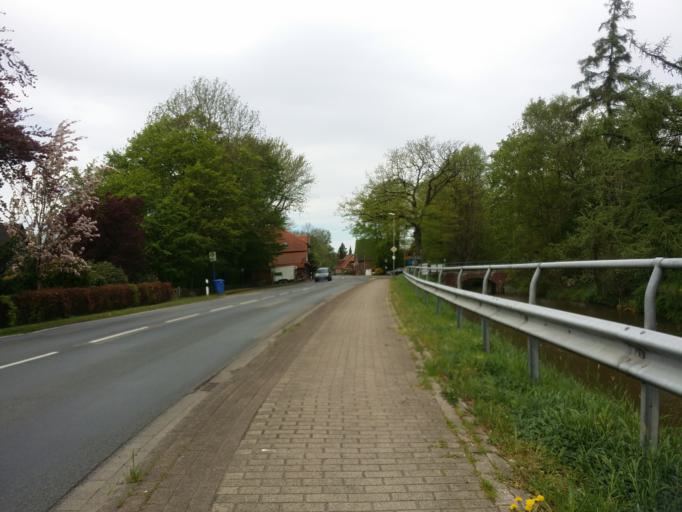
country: DE
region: Lower Saxony
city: Lemwerder
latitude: 53.1405
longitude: 8.5751
